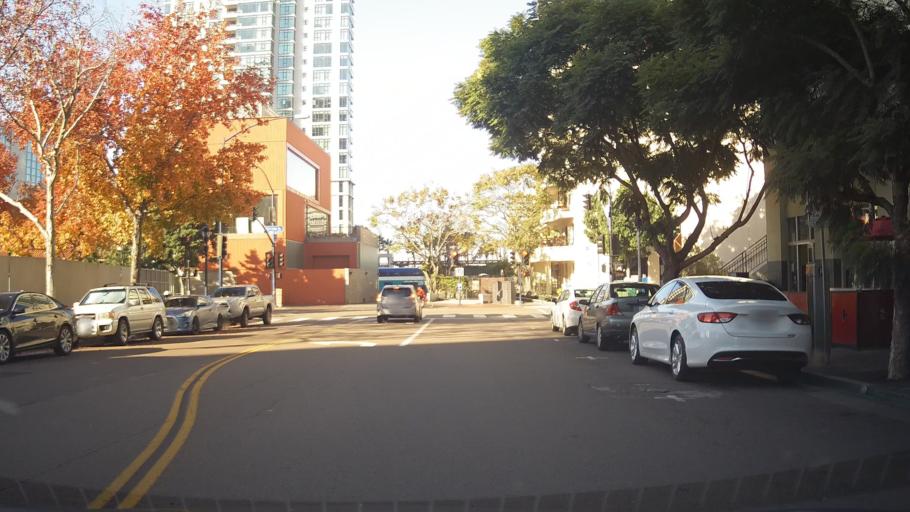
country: US
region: California
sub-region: San Diego County
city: San Diego
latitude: 32.7178
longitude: -117.1686
